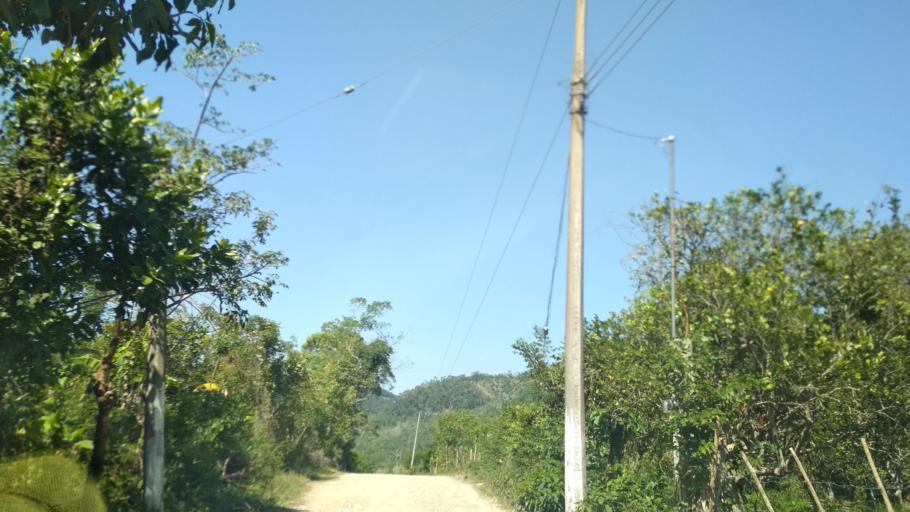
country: MX
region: Veracruz
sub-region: Papantla
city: Polutla
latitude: 20.4766
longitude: -97.2197
